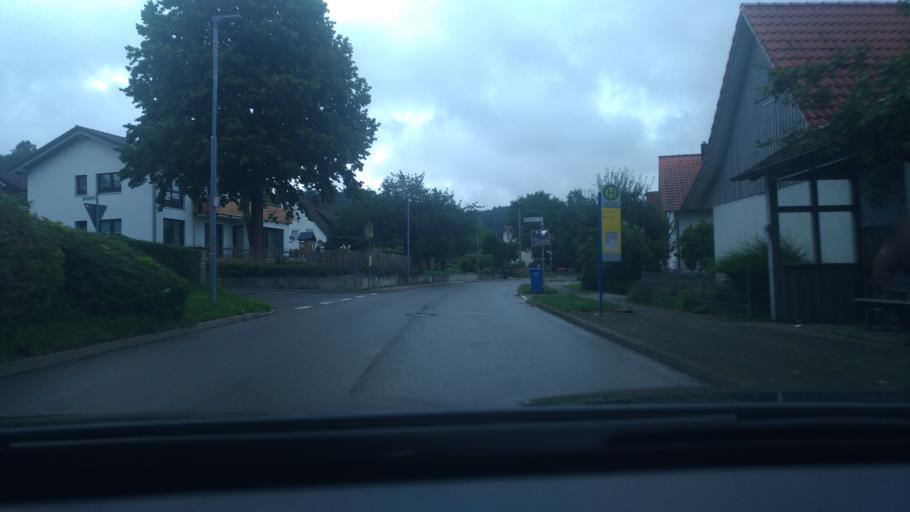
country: DE
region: Baden-Wuerttemberg
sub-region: Tuebingen Region
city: Sipplingen
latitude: 47.8168
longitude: 9.1185
